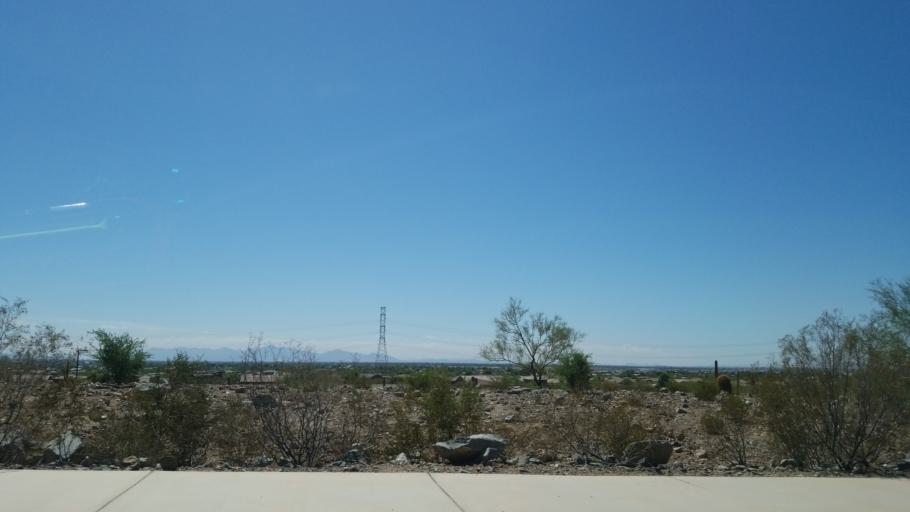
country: US
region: Arizona
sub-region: Maricopa County
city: Sun City West
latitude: 33.7104
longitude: -112.2453
